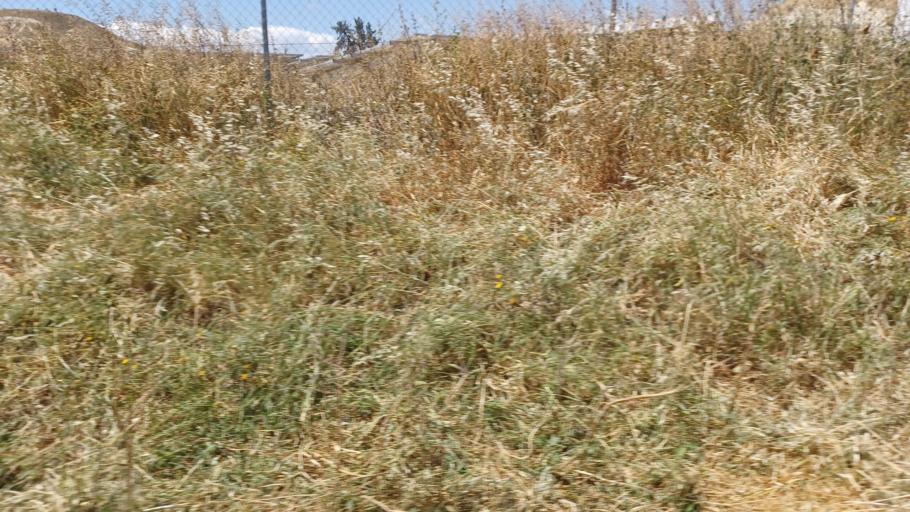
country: CY
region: Larnaka
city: Athienou
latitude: 35.0394
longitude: 33.5379
